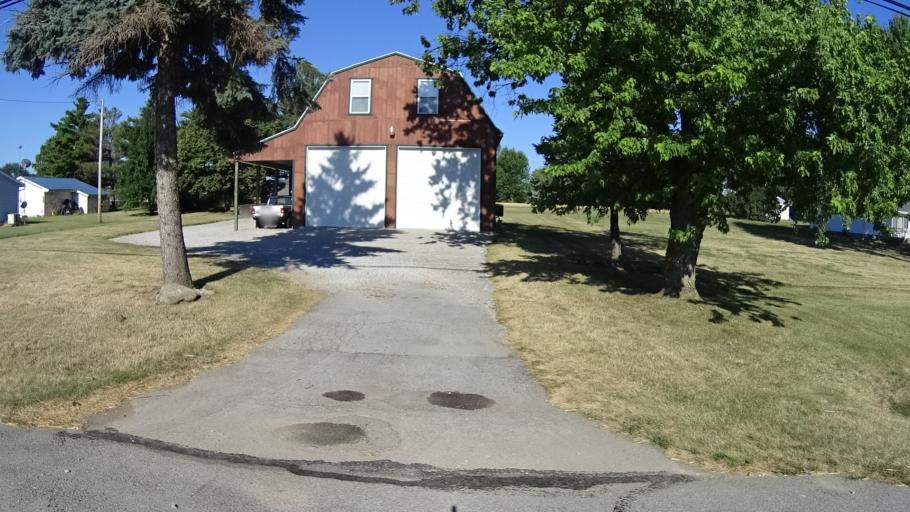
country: US
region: Ohio
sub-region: Erie County
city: Sandusky
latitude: 41.4015
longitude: -82.7712
